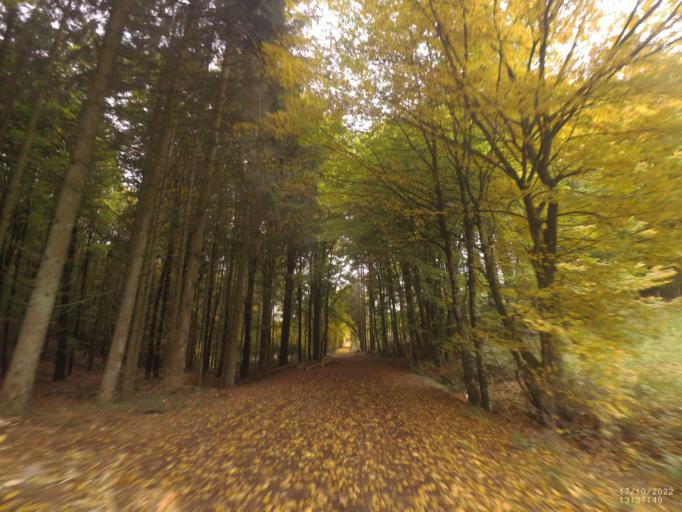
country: DE
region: Rheinland-Pfalz
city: Horscheid
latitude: 50.2210
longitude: 6.8726
